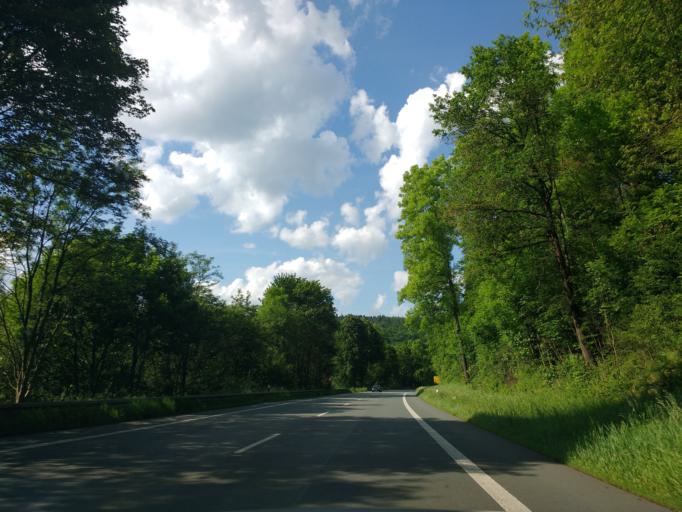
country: DE
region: Hesse
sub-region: Regierungsbezirk Kassel
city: Frankenau
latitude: 51.1252
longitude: 8.8734
